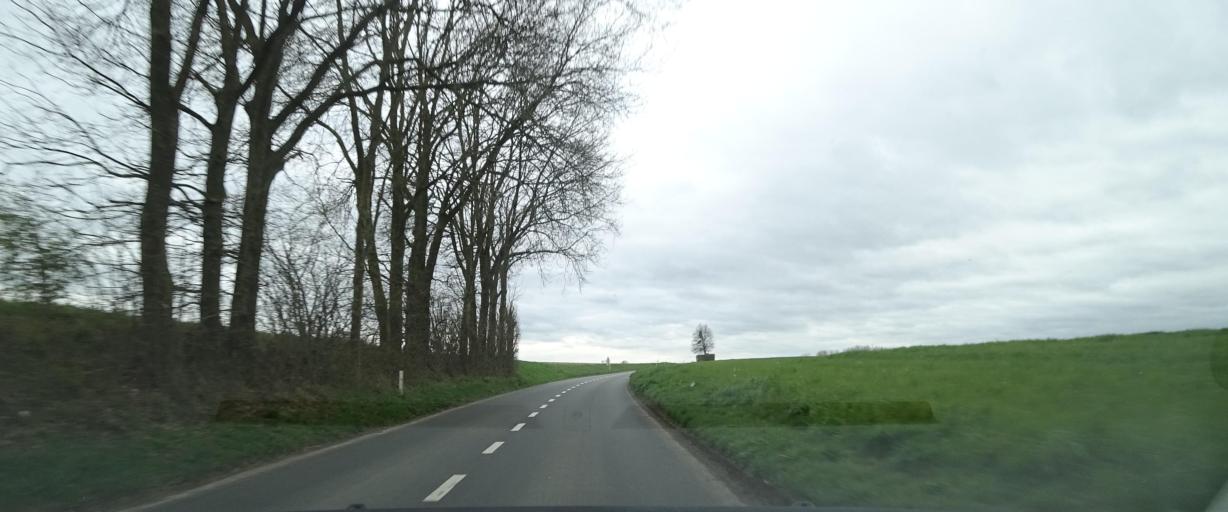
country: BE
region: Wallonia
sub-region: Province du Brabant Wallon
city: Walhain-Saint-Paul
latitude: 50.6348
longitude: 4.7189
